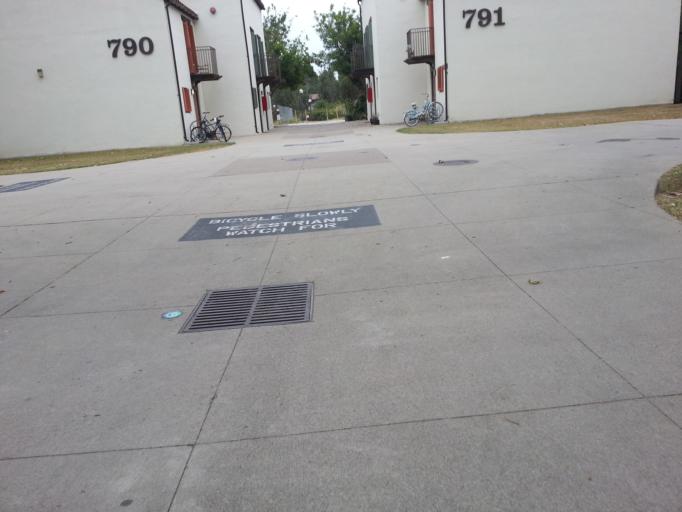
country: US
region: California
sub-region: Santa Barbara County
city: Isla Vista
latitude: 34.4220
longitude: -119.8626
